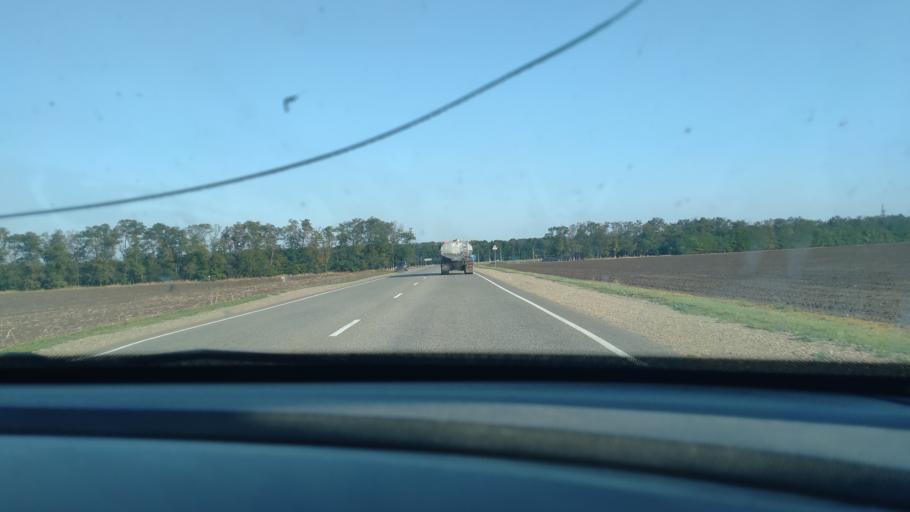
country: RU
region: Krasnodarskiy
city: Starominskaya
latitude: 46.4962
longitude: 39.0529
